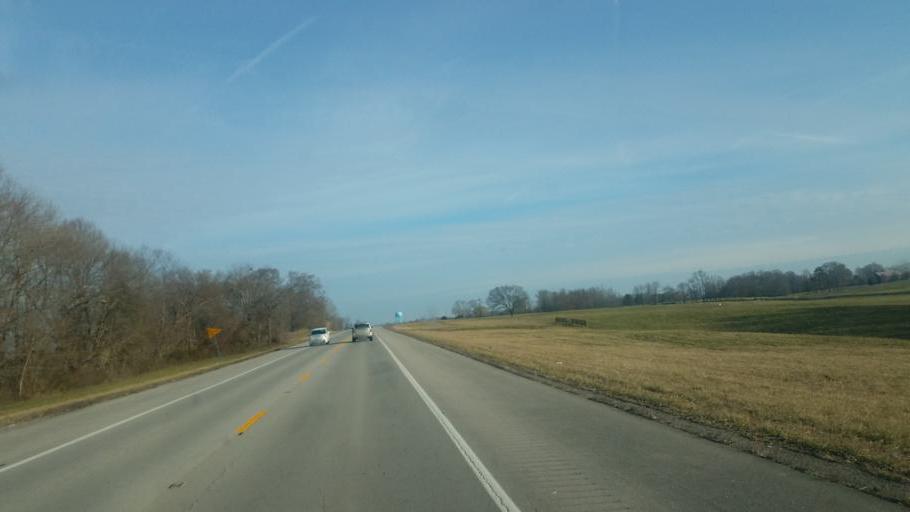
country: US
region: Kentucky
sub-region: Russell County
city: Jamestown
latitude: 36.9874
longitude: -85.0847
